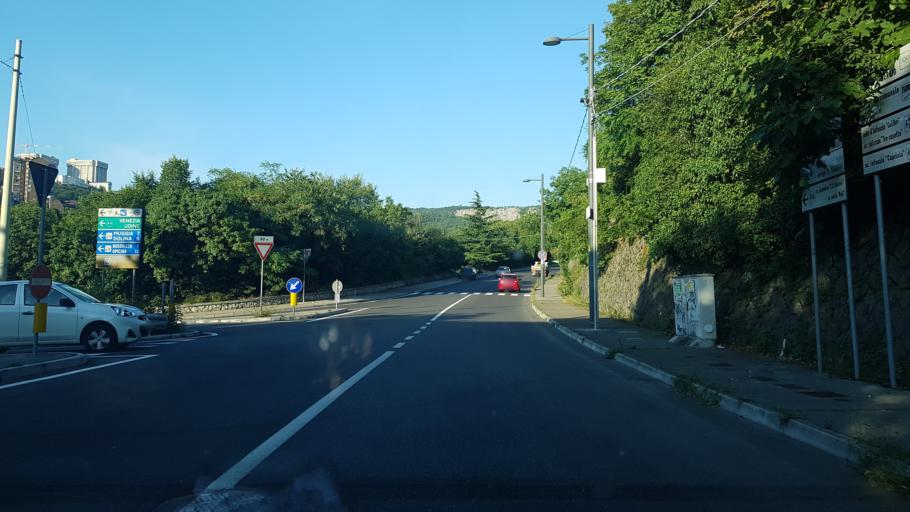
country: IT
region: Friuli Venezia Giulia
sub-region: Provincia di Trieste
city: Domio
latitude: 45.6215
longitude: 13.8171
